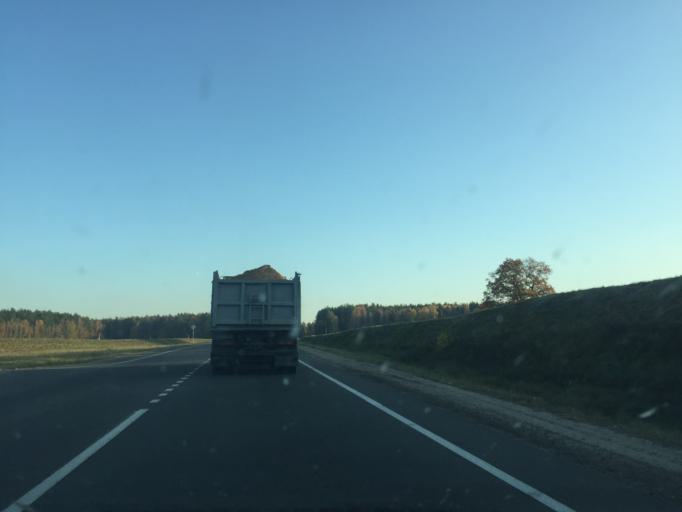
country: BY
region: Mogilev
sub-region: Mahilyowski Rayon
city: Kadino
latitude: 53.8984
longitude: 30.4794
